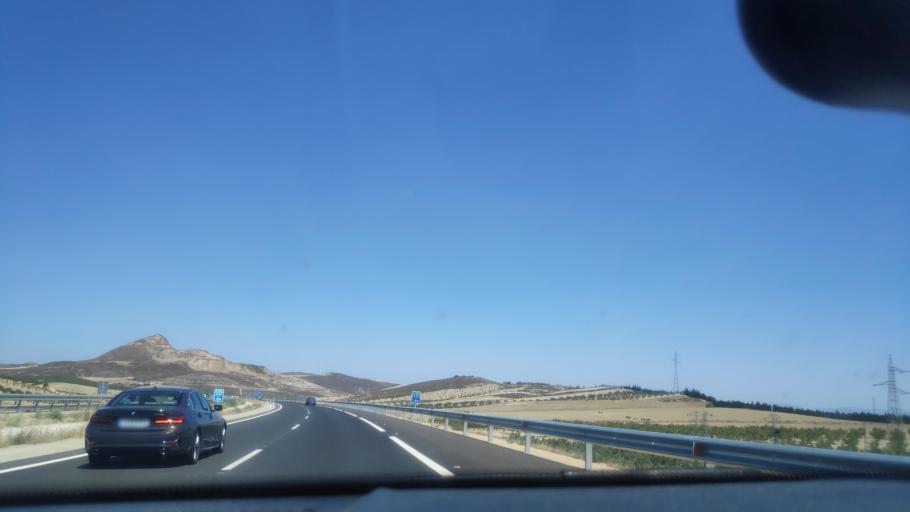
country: ES
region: Andalusia
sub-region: Provincia de Granada
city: Alhendin
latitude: 37.0870
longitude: -3.6669
